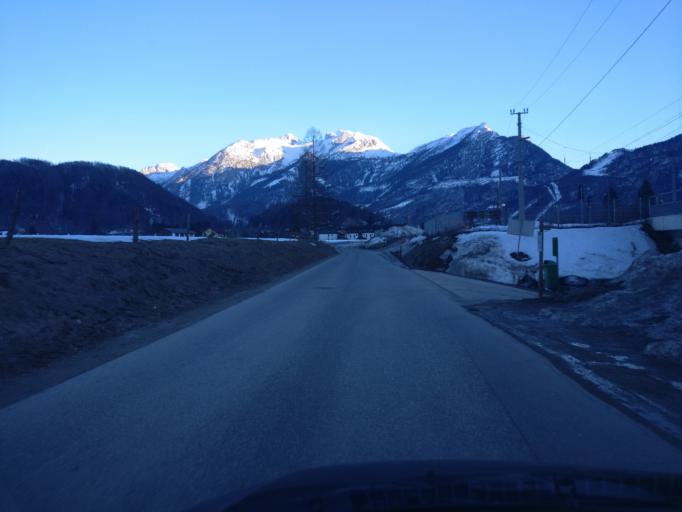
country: AT
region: Salzburg
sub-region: Politischer Bezirk Hallein
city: Golling an der Salzach
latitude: 47.6056
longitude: 13.1620
